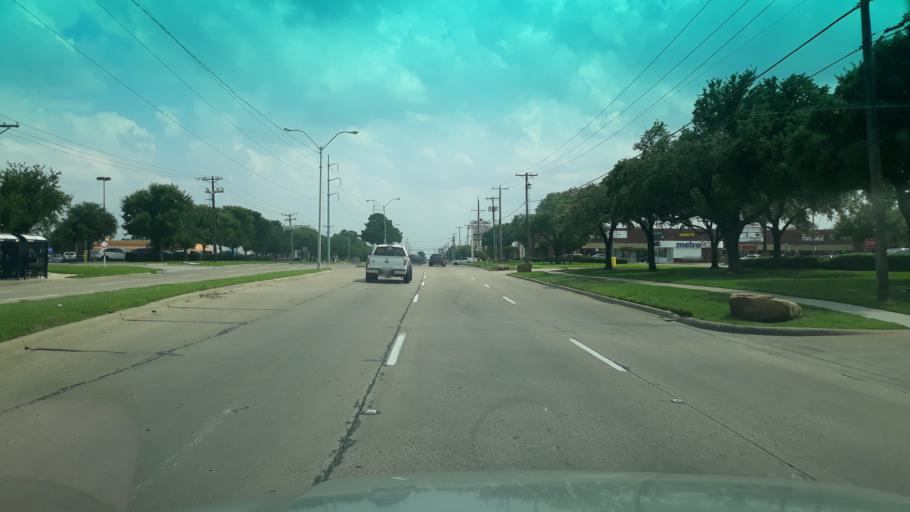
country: US
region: Texas
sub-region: Dallas County
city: Irving
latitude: 32.8562
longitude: -96.9922
